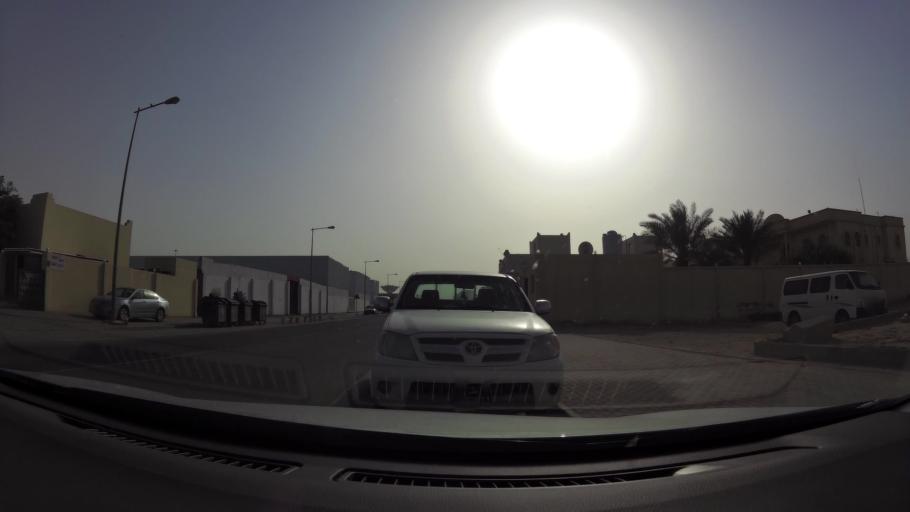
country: QA
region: Baladiyat ar Rayyan
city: Ar Rayyan
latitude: 25.2338
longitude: 51.4432
